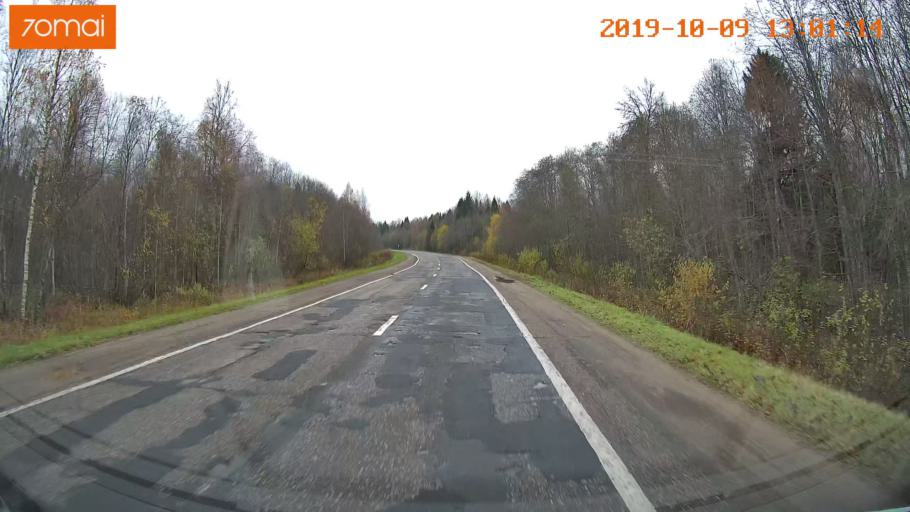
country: RU
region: Jaroslavl
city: Prechistoye
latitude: 58.3700
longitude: 40.4848
